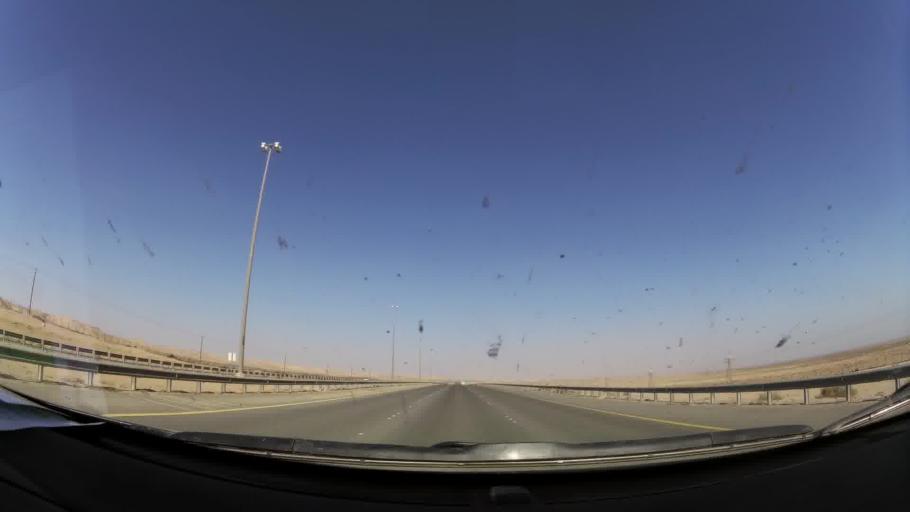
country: KW
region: Muhafazat al Jahra'
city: Al Jahra'
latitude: 29.4981
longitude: 47.7928
